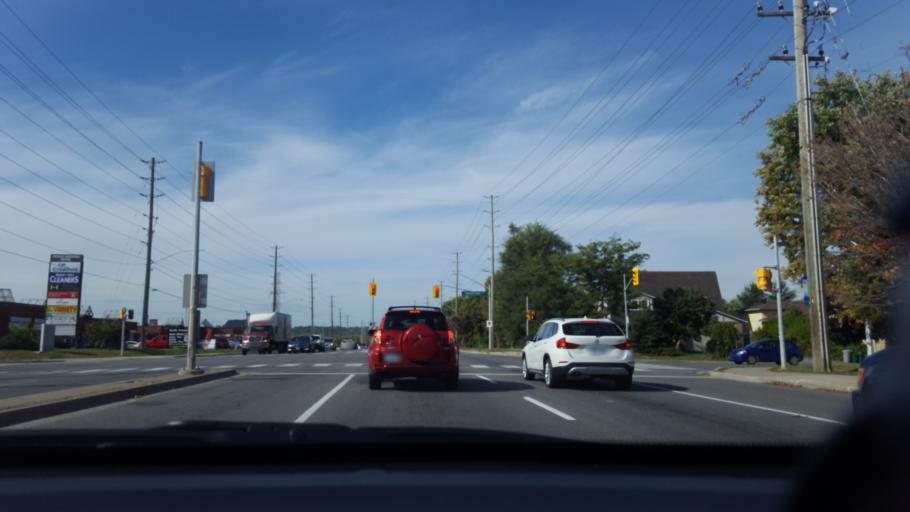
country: CA
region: Ontario
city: Newmarket
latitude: 44.0380
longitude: -79.4686
